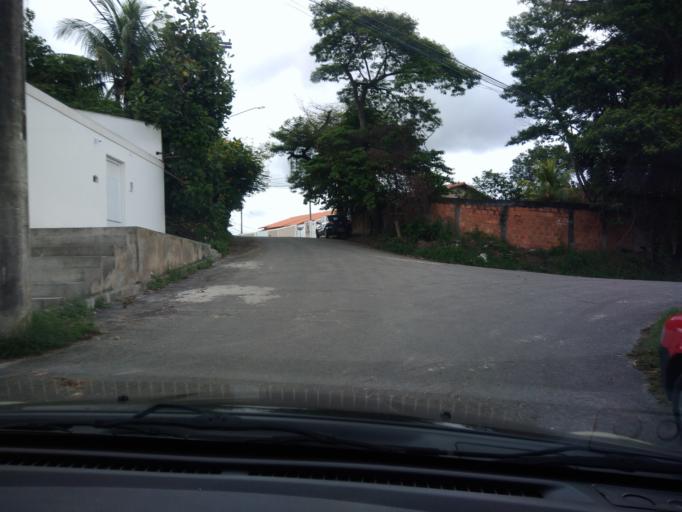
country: BR
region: Rio de Janeiro
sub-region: Niteroi
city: Niteroi
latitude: -22.9316
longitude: -43.0114
